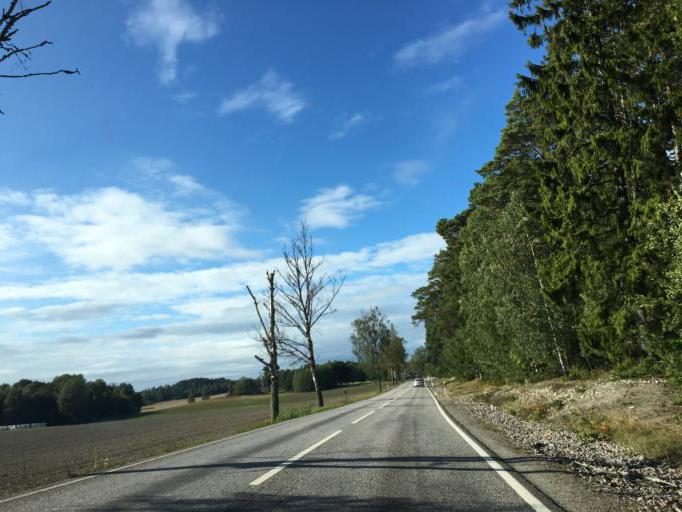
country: SE
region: Soedermanland
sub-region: Nykopings Kommun
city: Stigtomta
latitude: 58.8665
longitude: 16.9035
